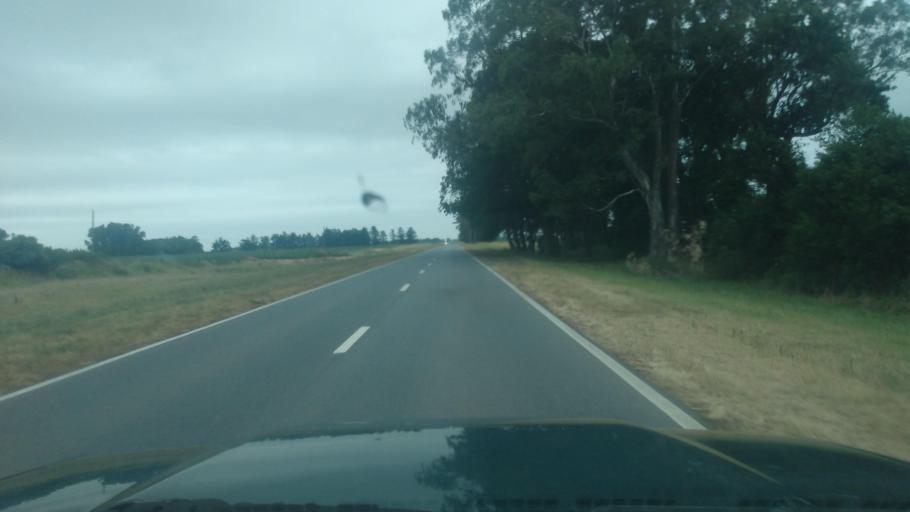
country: AR
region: Buenos Aires
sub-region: Partido de Bragado
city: Bragado
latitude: -35.2734
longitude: -60.5832
